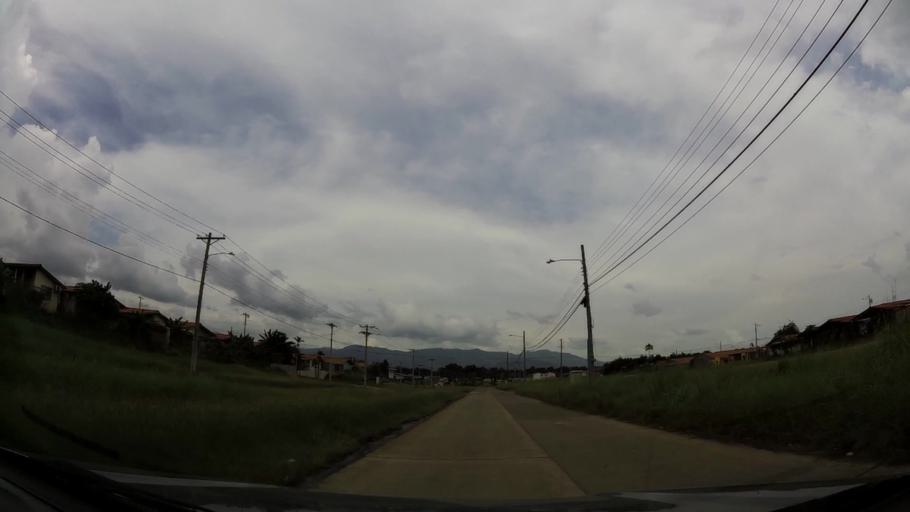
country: PA
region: Panama
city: Cabra Numero Uno
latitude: 9.1161
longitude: -79.3199
